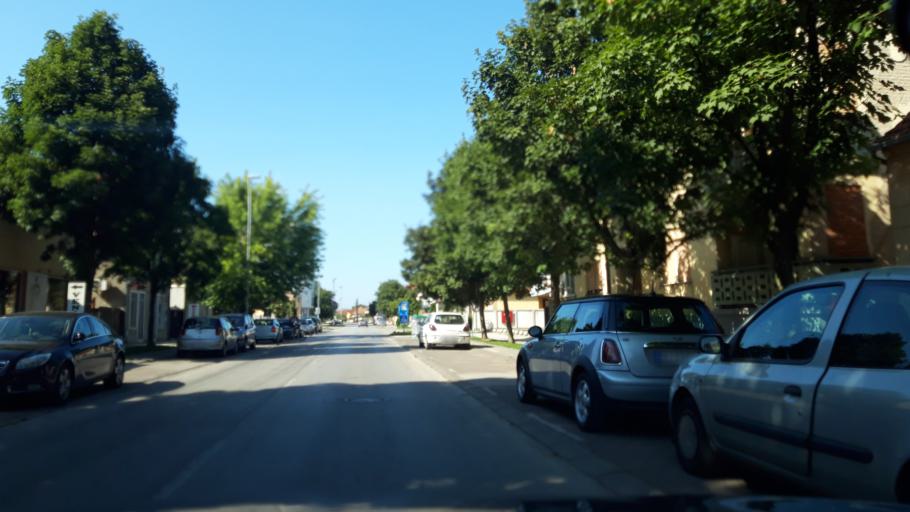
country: RS
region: Autonomna Pokrajina Vojvodina
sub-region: Sremski Okrug
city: Ruma
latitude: 45.0128
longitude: 19.8226
